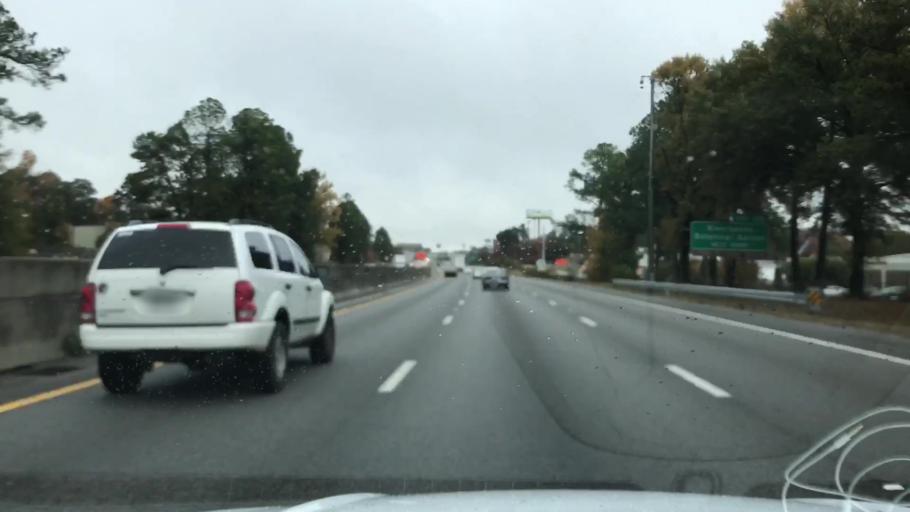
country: US
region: South Carolina
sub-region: Lexington County
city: Springdale
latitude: 33.9927
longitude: -81.1076
